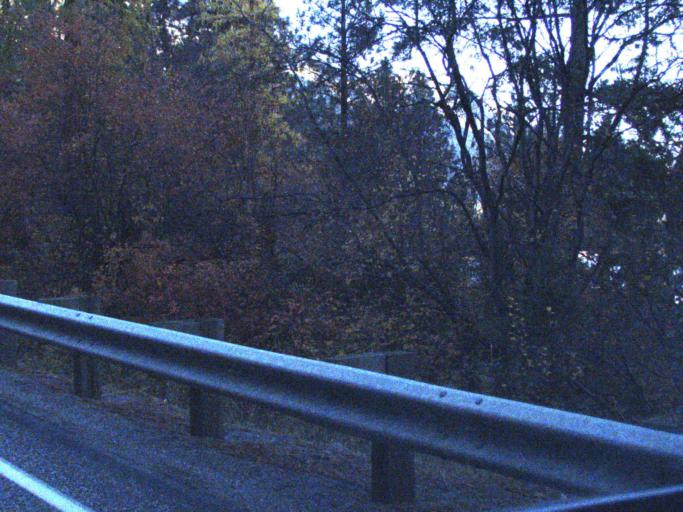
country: CA
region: British Columbia
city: Rossland
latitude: 48.8728
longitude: -117.8473
